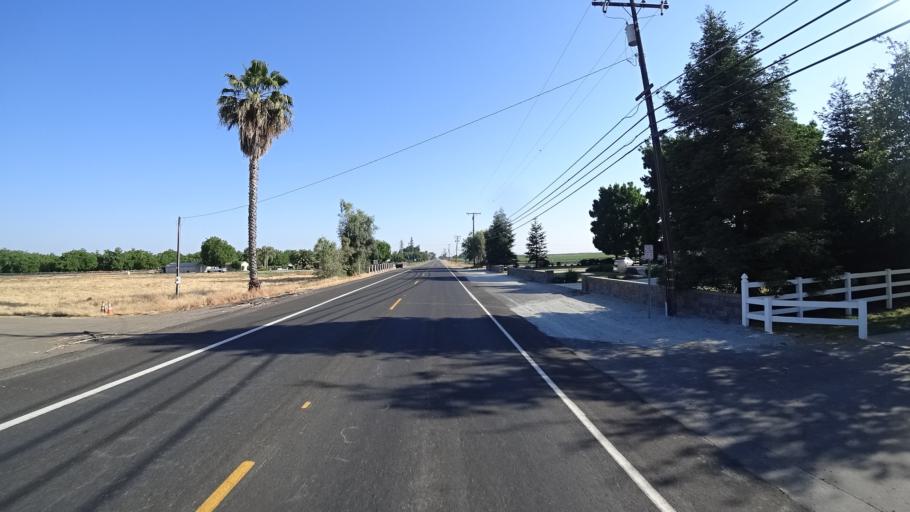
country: US
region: California
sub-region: Kings County
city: Armona
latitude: 36.3492
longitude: -119.7090
